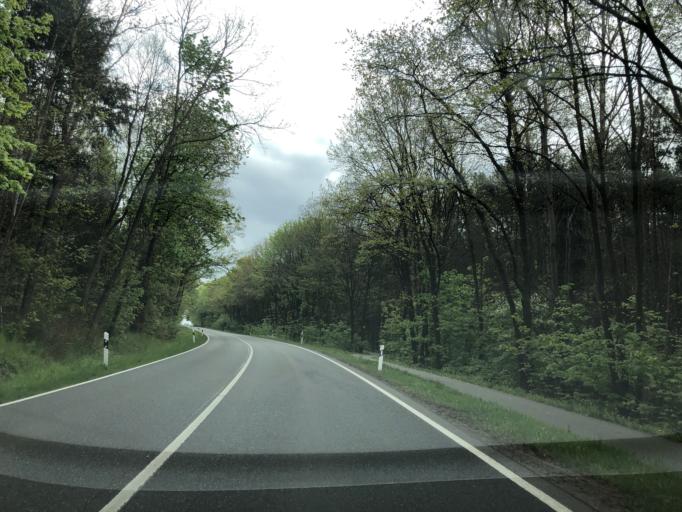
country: DE
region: Mecklenburg-Vorpommern
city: Plau am See
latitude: 53.4652
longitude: 12.1951
